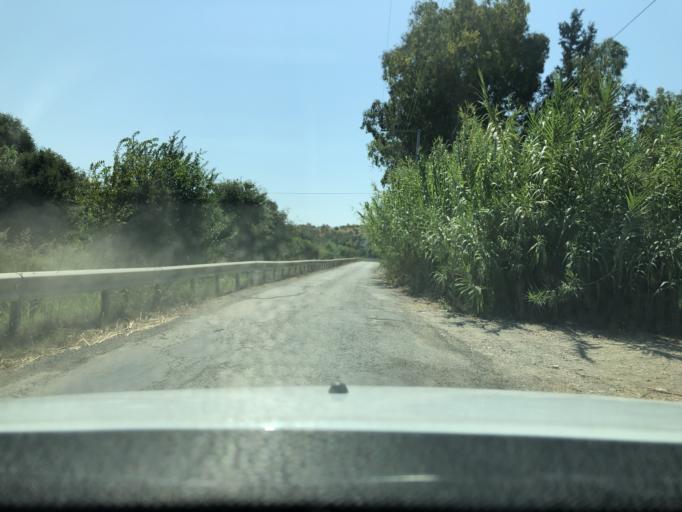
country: TR
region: Antalya
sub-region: Manavgat
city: Manavgat
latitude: 36.8042
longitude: 31.4677
